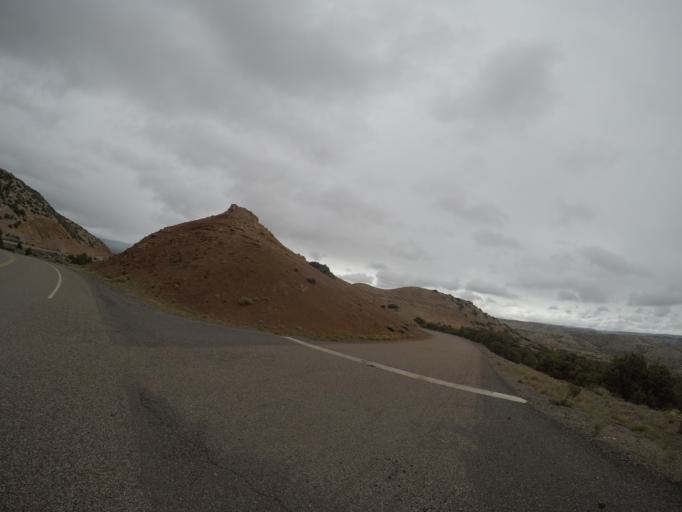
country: US
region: Wyoming
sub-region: Big Horn County
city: Lovell
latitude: 45.0359
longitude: -108.2578
